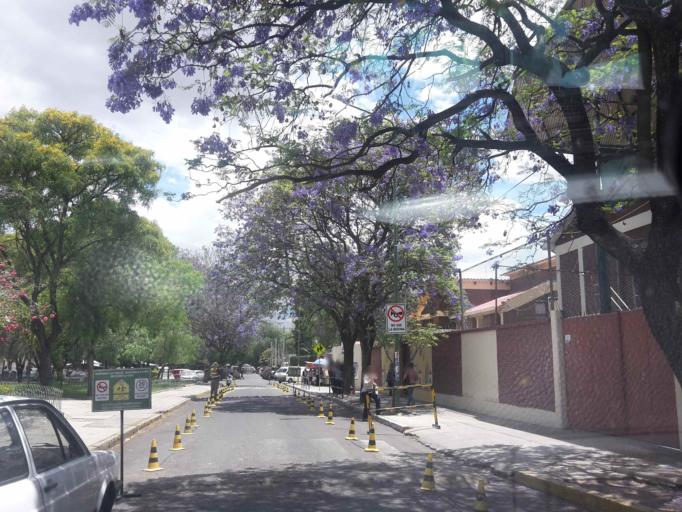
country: BO
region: Cochabamba
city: Cochabamba
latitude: -17.3878
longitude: -66.1465
